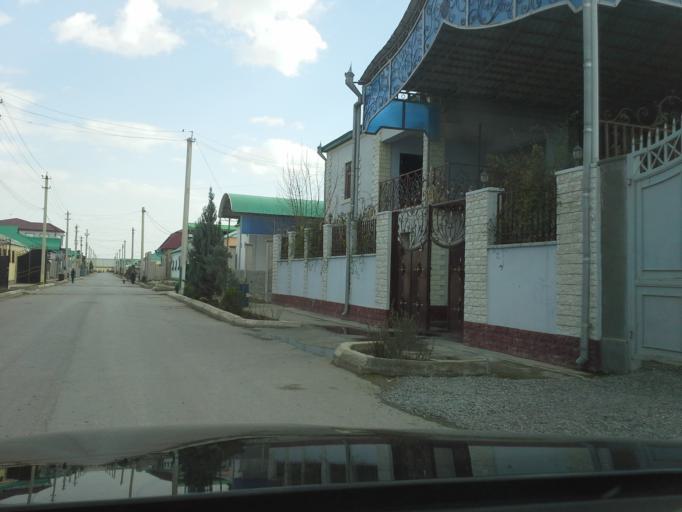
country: TM
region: Ahal
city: Ashgabat
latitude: 37.9943
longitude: 58.2949
